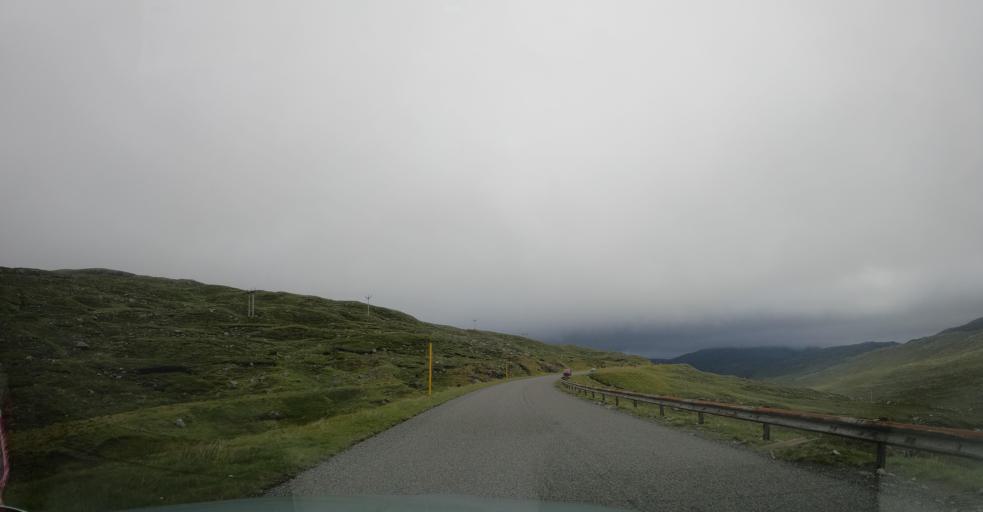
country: GB
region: Scotland
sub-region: Eilean Siar
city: Harris
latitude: 57.9561
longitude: -6.7686
